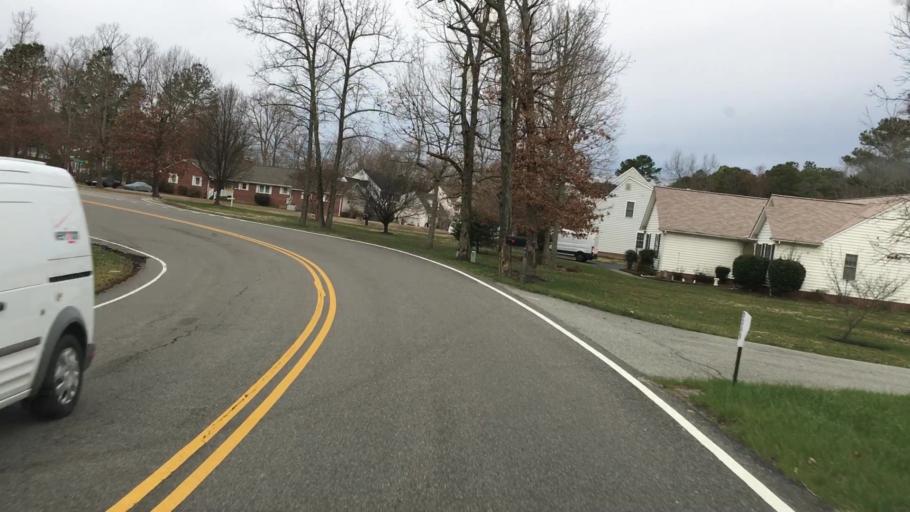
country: US
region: Virginia
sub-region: Henrico County
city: Glen Allen
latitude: 37.6736
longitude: -77.5540
